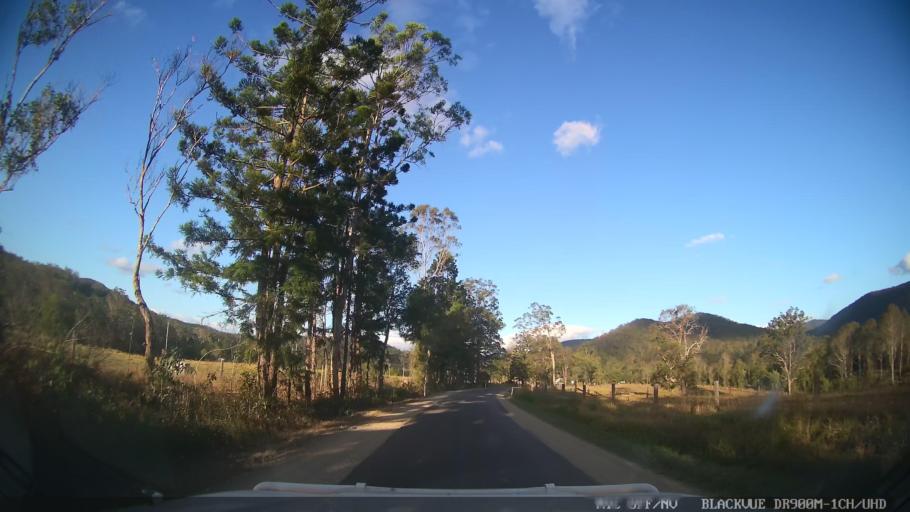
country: AU
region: Queensland
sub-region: Sunshine Coast
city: Nambour
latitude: -26.6283
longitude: 152.6839
